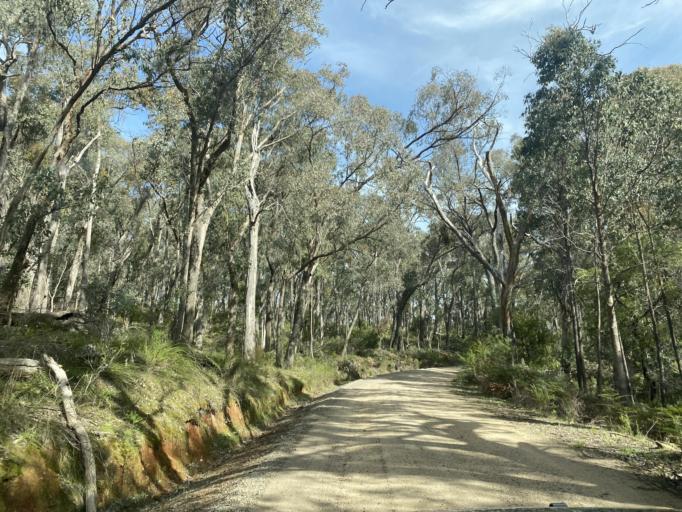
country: AU
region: Victoria
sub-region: Mansfield
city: Mansfield
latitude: -36.8253
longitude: 146.1525
